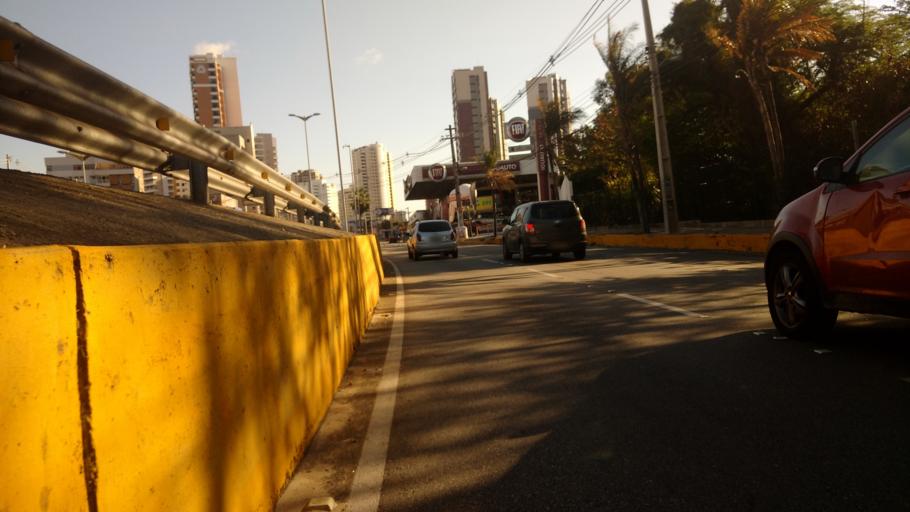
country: BR
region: Ceara
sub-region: Fortaleza
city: Fortaleza
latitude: -3.7558
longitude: -38.4915
